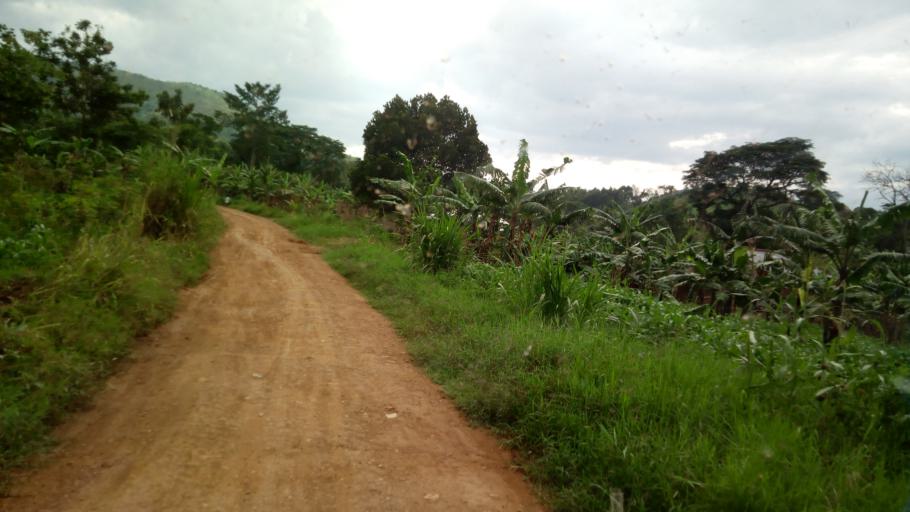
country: UG
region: Central Region
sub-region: Kiboga District
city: Kiboga
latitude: 0.7275
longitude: 31.7350
